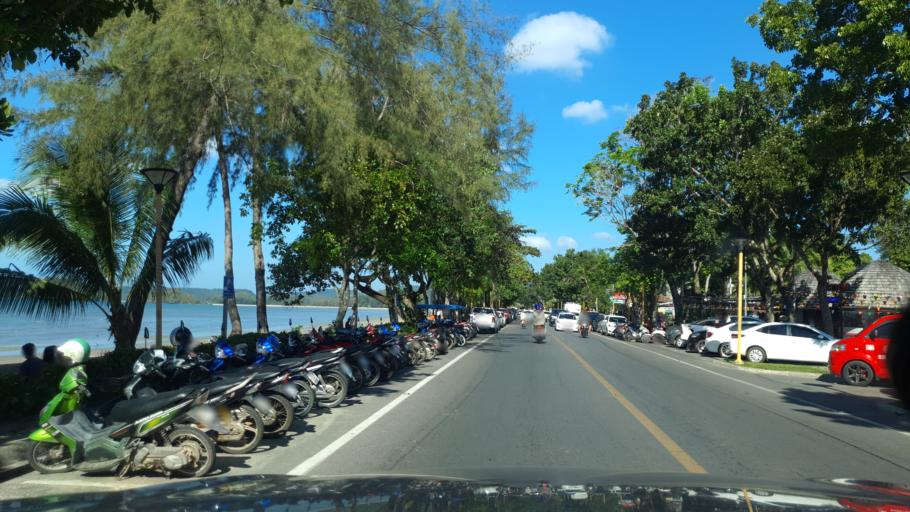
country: TH
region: Phangnga
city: Ban Ao Nang
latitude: 8.0399
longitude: 98.8148
